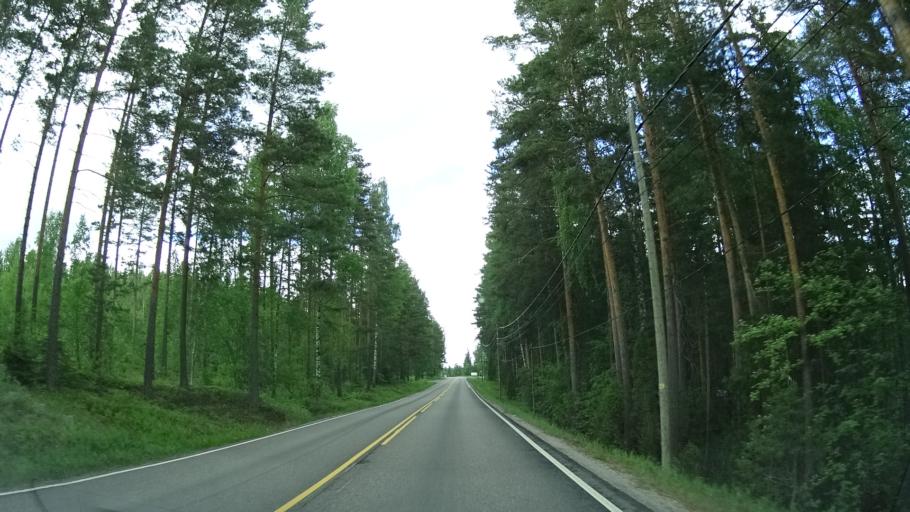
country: FI
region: Paijanne Tavastia
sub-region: Lahti
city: Asikkala
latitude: 61.3295
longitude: 25.5706
